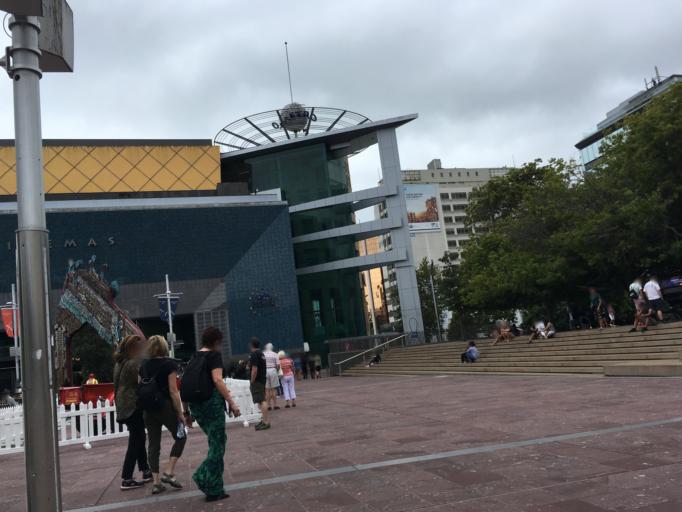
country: NZ
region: Auckland
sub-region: Auckland
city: Auckland
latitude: -36.8523
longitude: 174.7634
